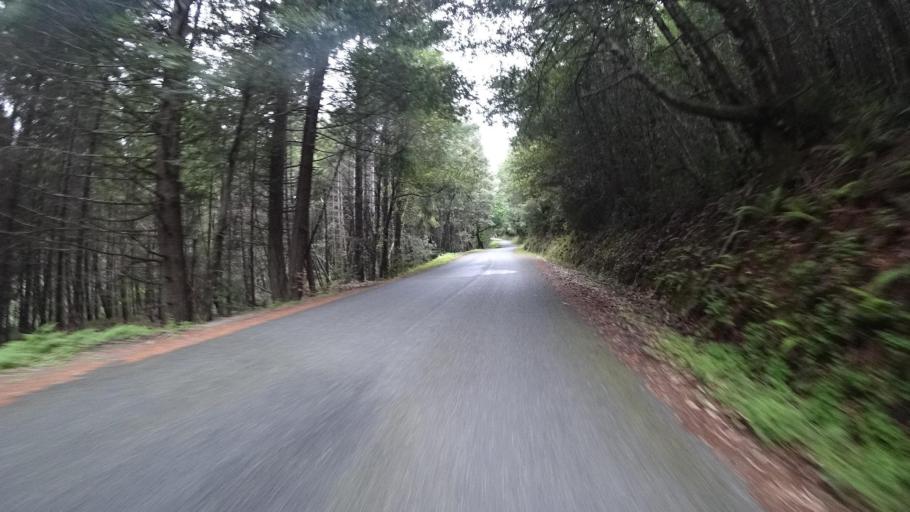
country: US
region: California
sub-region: Humboldt County
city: Willow Creek
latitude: 41.2004
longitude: -123.7554
